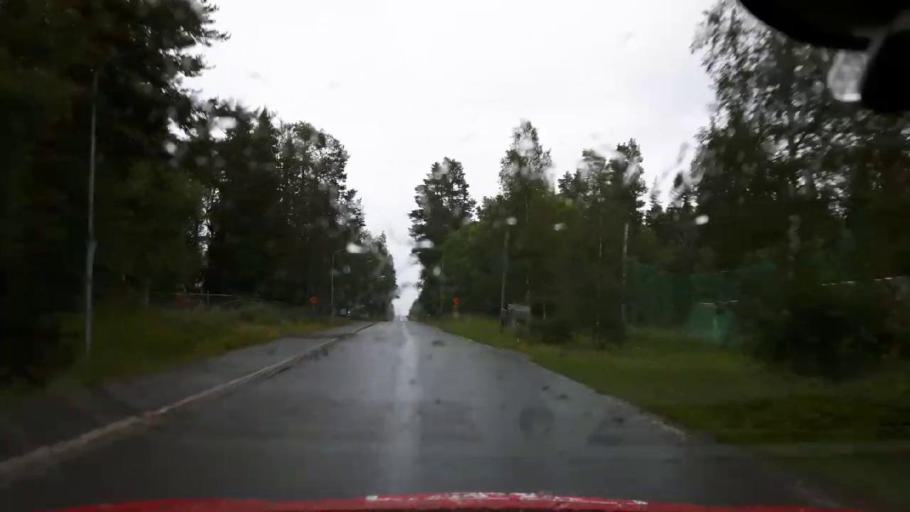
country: SE
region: Jaemtland
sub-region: OEstersunds Kommun
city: Brunflo
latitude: 63.0005
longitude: 14.7502
